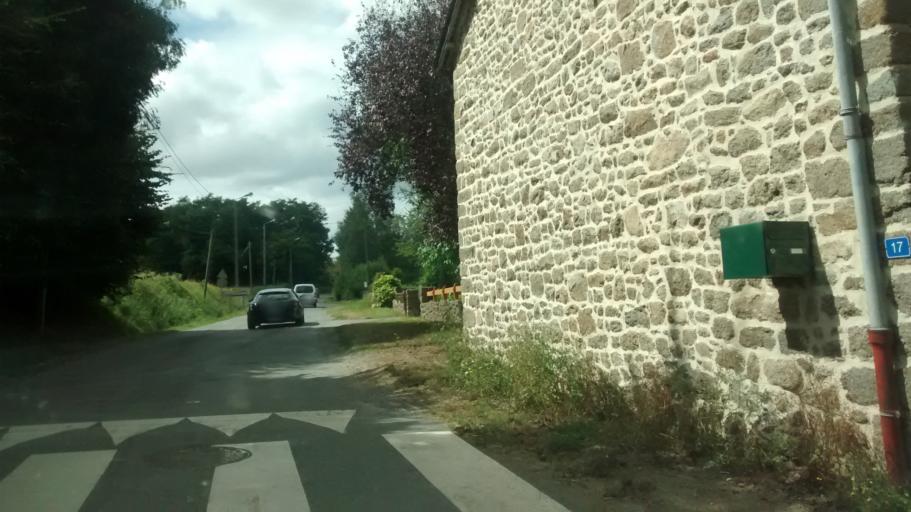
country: FR
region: Brittany
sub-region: Departement d'Ille-et-Vilaine
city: Hede-Bazouges
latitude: 48.2914
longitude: -1.8262
